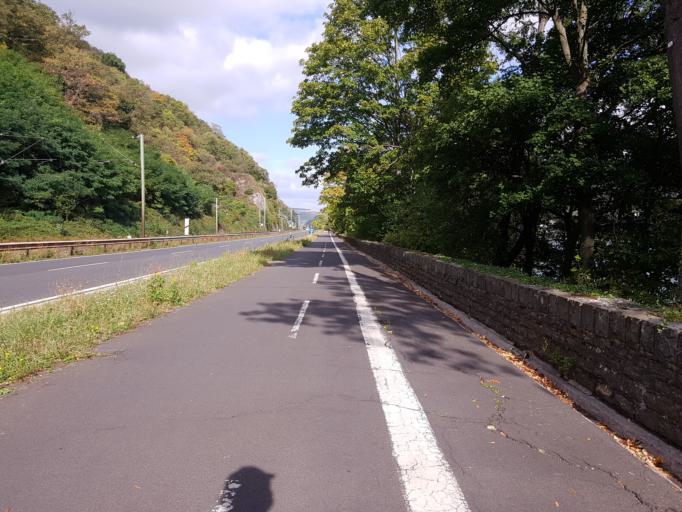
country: DE
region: Rheinland-Pfalz
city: Kaub
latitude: 50.0766
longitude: 7.7694
